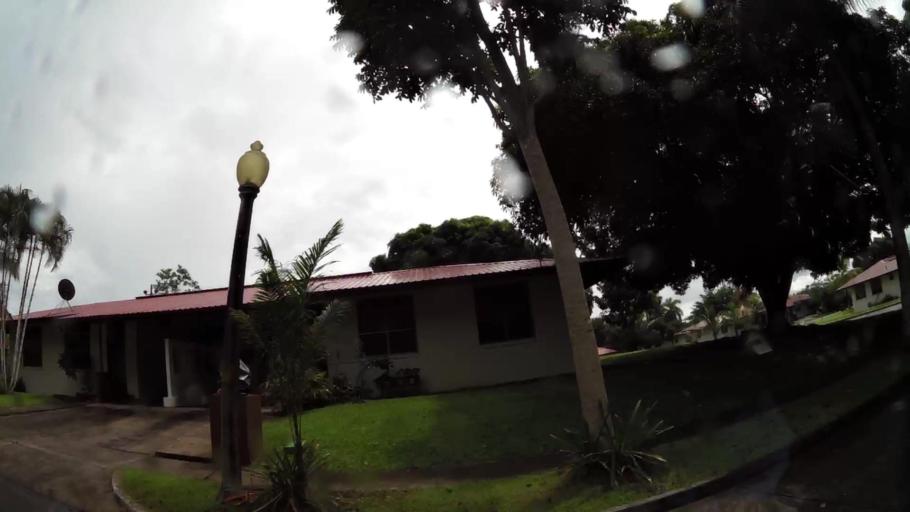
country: PA
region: Panama
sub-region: Distrito de Panama
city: Paraiso
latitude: 9.0057
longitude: -79.5813
